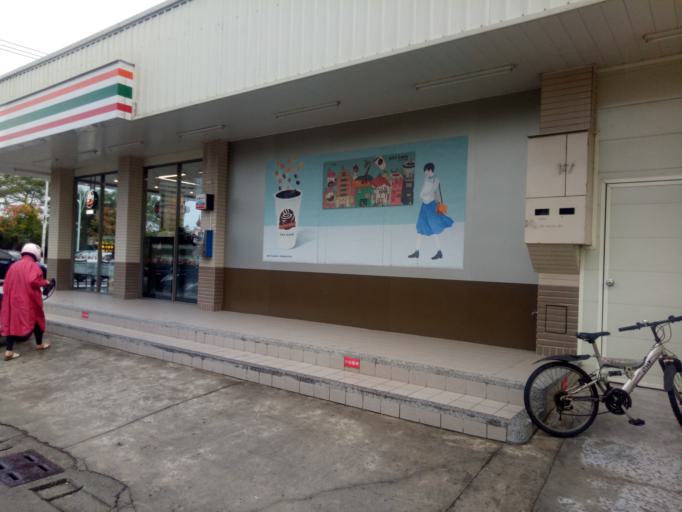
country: TW
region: Taiwan
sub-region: Taichung City
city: Taichung
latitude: 24.2432
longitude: 120.5434
